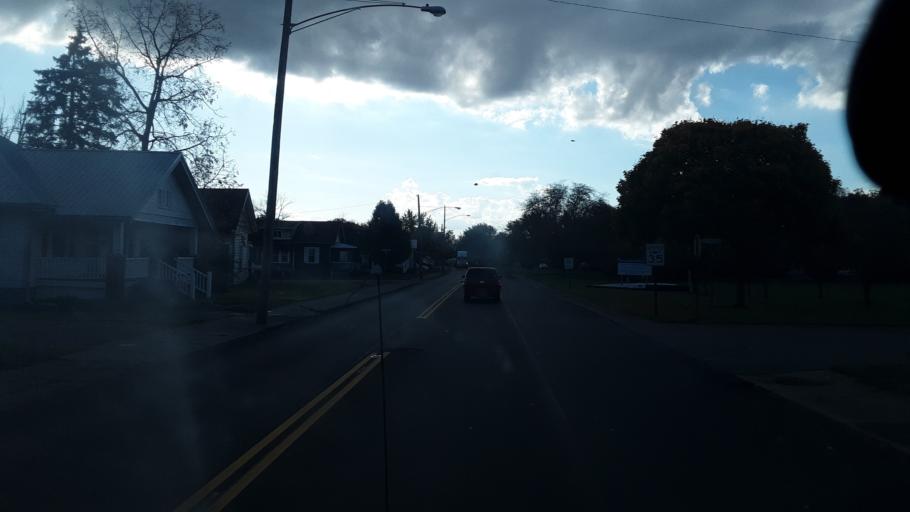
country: US
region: Ohio
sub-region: Fayette County
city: Washington Court House
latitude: 39.5454
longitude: -83.4464
